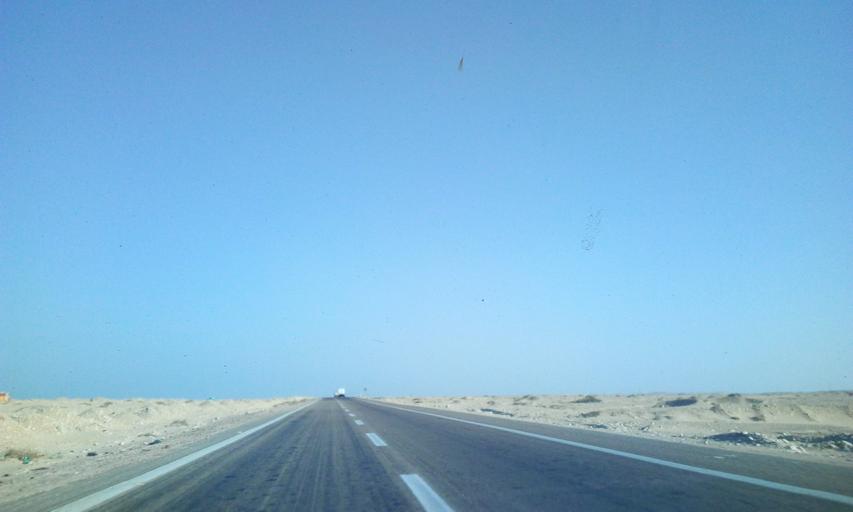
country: EG
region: As Suways
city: Ain Sukhna
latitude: 28.8358
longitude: 32.7088
